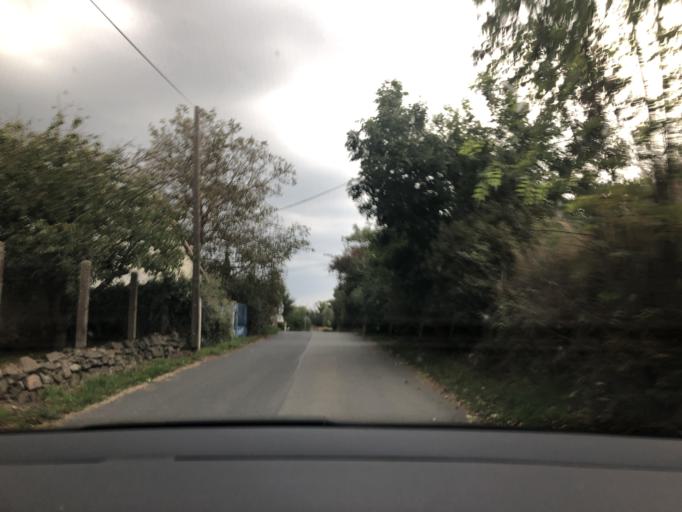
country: CZ
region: Central Bohemia
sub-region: Okres Kolin
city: Tynec nad Labem
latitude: 50.0365
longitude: 15.3638
